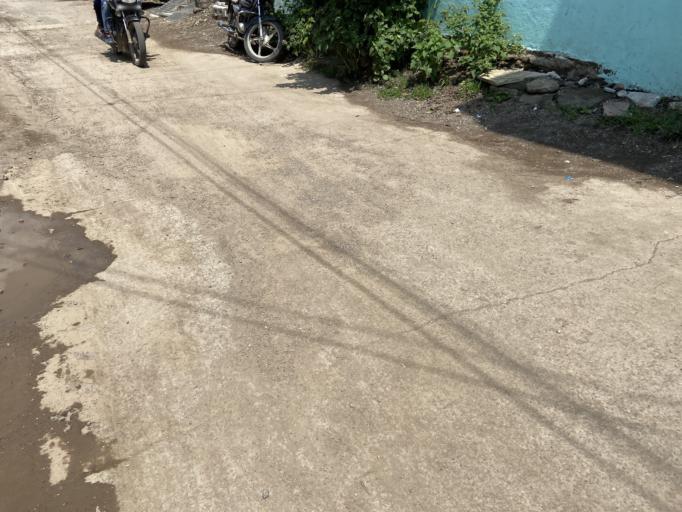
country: IN
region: Maharashtra
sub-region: Aurangabad Division
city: Khuldabad
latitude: 19.9356
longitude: 75.2253
